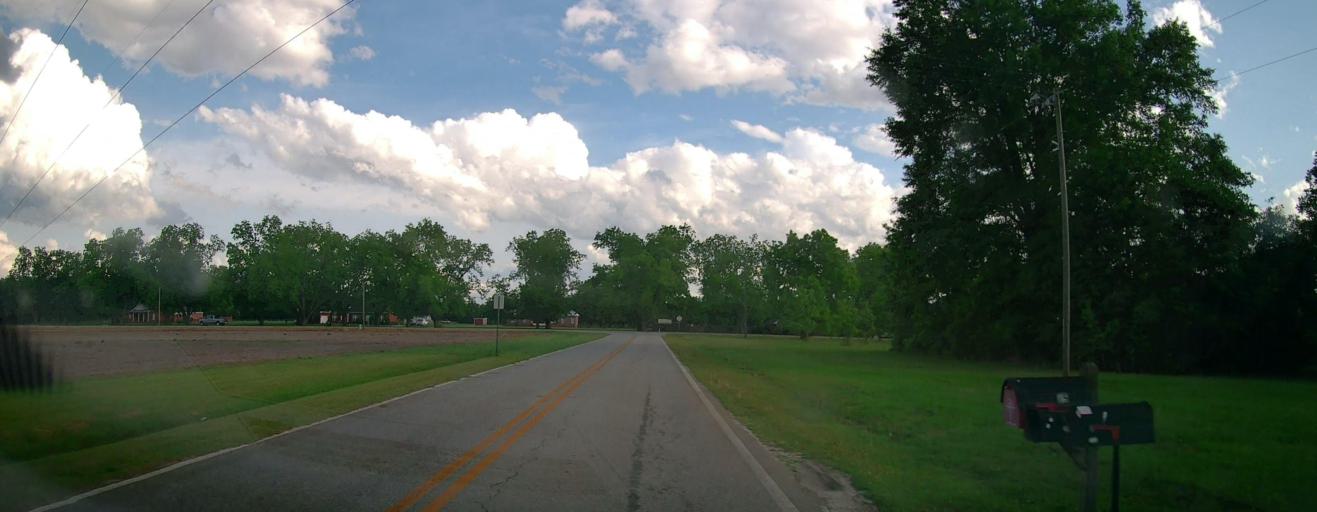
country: US
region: Georgia
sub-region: Peach County
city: Byron
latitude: 32.6530
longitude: -83.7882
